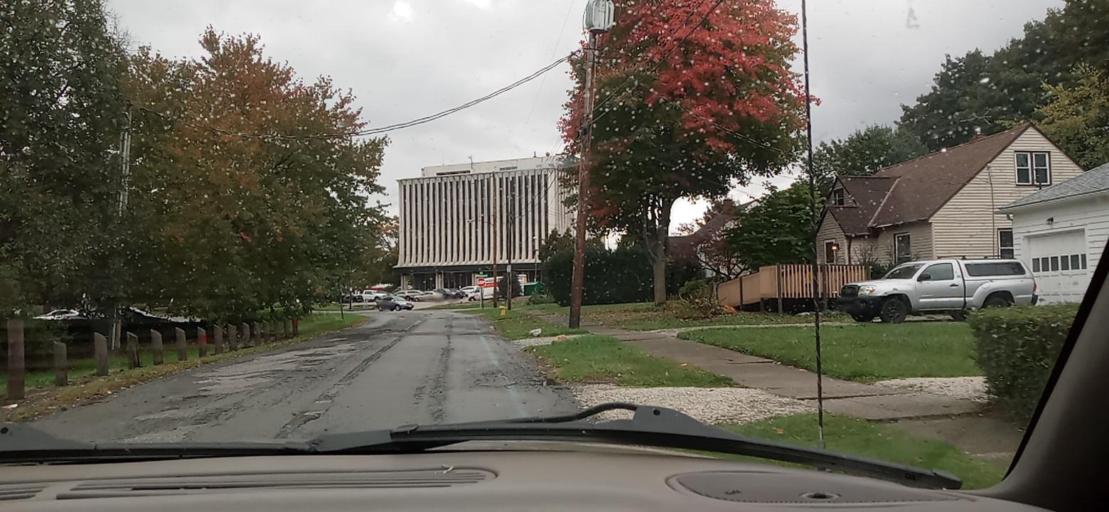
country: US
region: Ohio
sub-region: Summit County
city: Fairlawn
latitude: 41.1111
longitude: -81.5682
